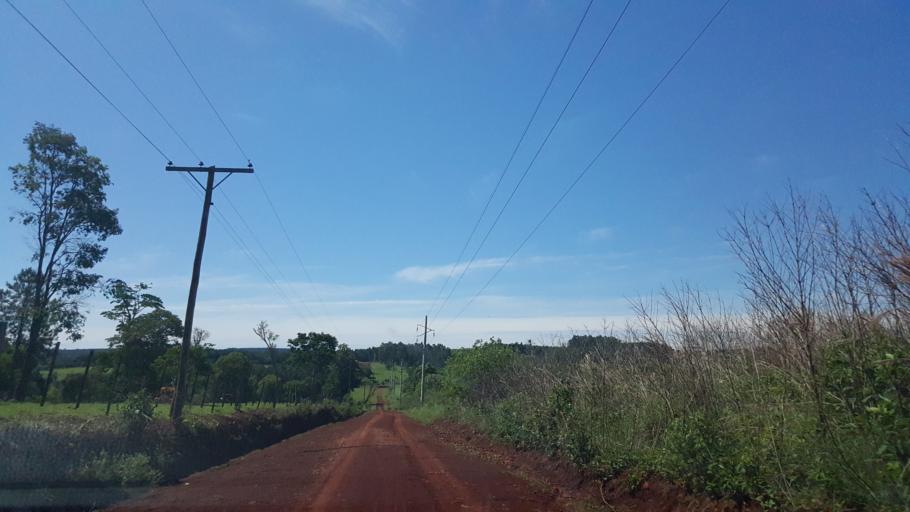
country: AR
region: Misiones
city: Capiovi
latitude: -26.9248
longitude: -55.0719
